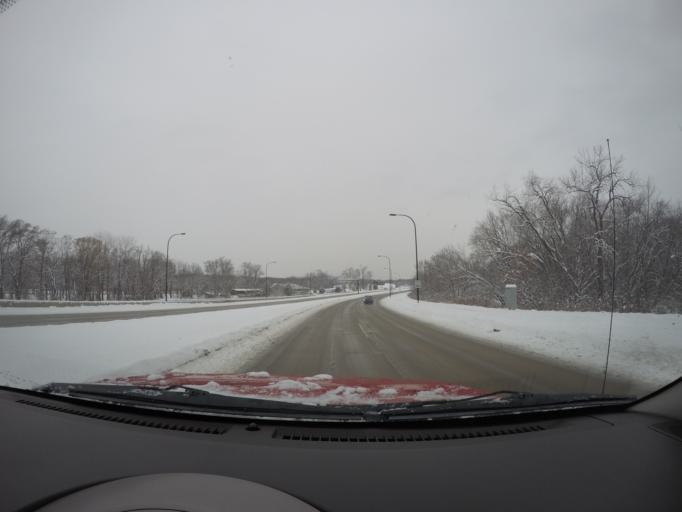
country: US
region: Wisconsin
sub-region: La Crosse County
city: La Crosse
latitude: 43.8108
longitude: -91.2640
